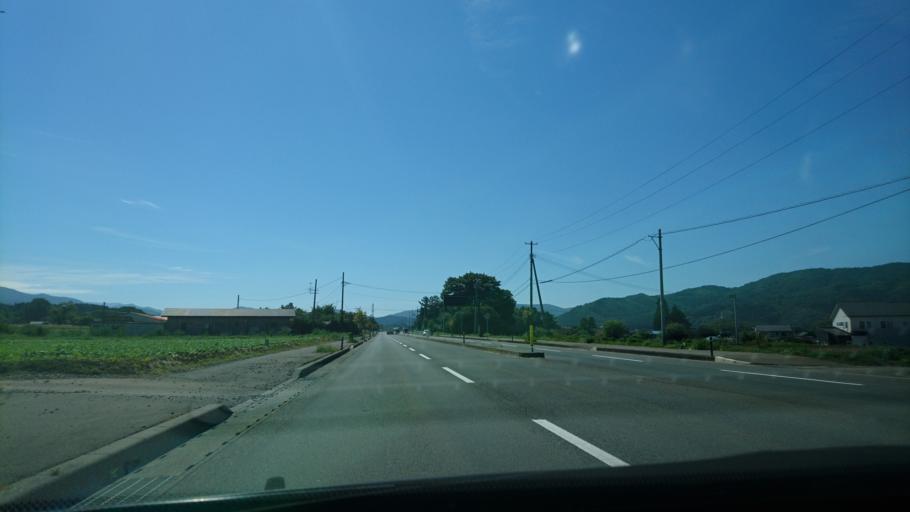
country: JP
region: Iwate
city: Tono
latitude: 39.3204
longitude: 141.5667
